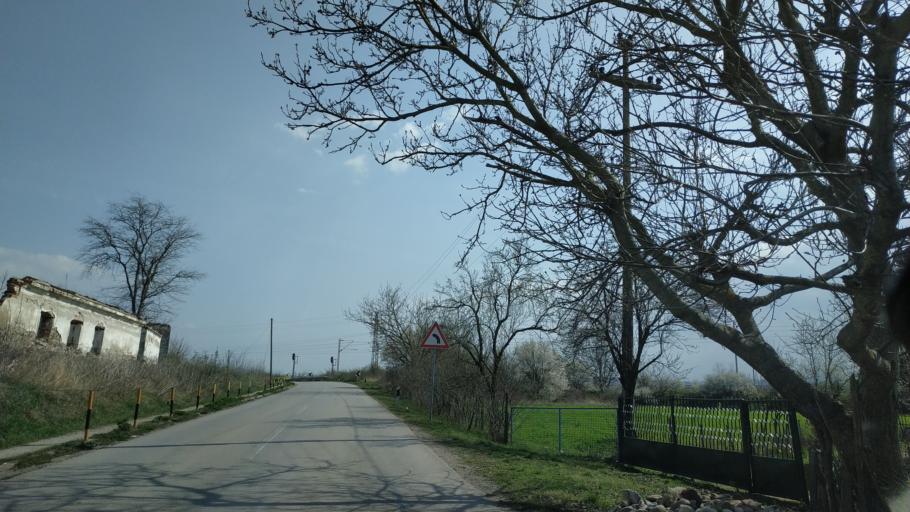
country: RS
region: Central Serbia
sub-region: Nisavski Okrug
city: Aleksinac
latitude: 43.5153
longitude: 21.6742
